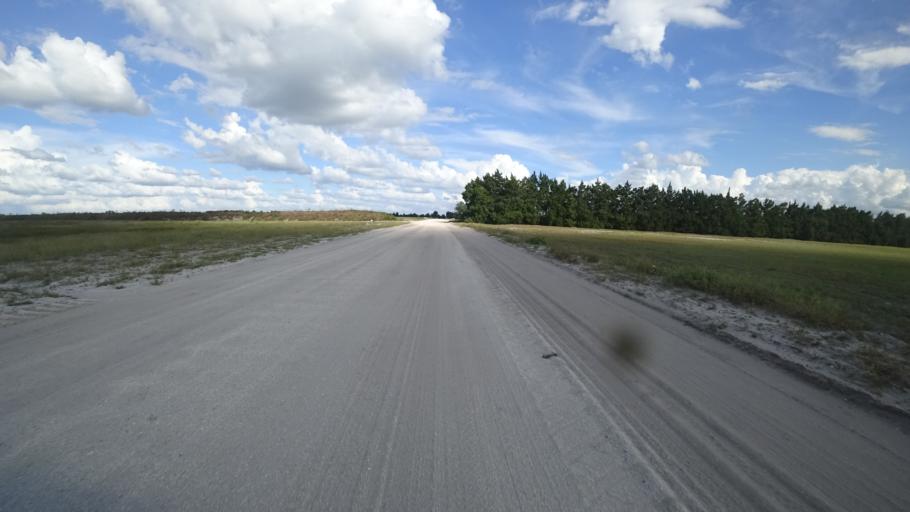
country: US
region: Florida
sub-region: DeSoto County
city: Arcadia
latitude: 27.2992
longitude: -82.1187
